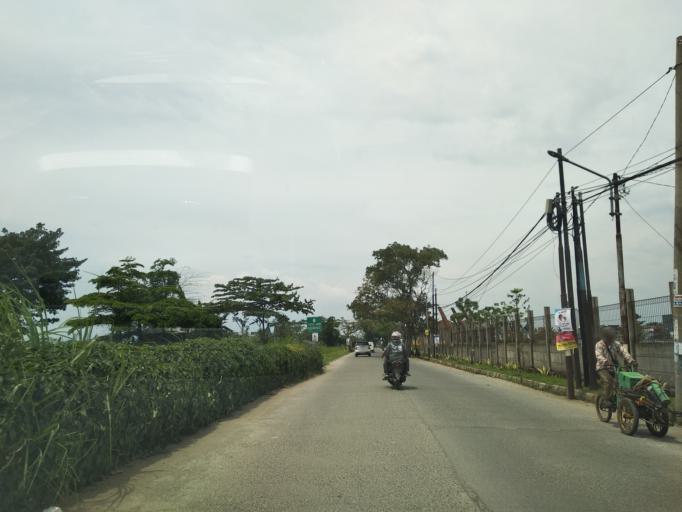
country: ID
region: West Java
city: Pameungpeuk
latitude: -6.9708
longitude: 107.6418
